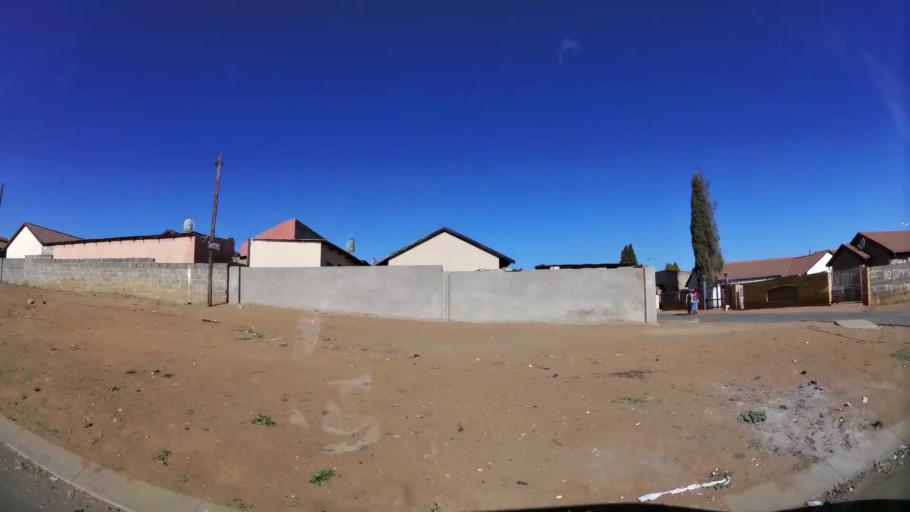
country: ZA
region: Gauteng
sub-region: Ekurhuleni Metropolitan Municipality
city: Tembisa
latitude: -26.0280
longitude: 28.2182
